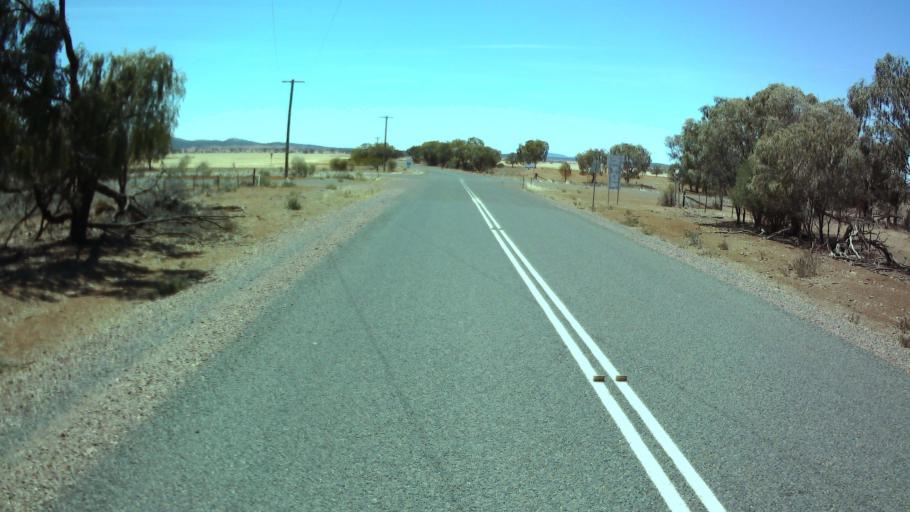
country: AU
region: New South Wales
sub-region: Forbes
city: Forbes
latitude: -33.6741
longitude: 147.6736
